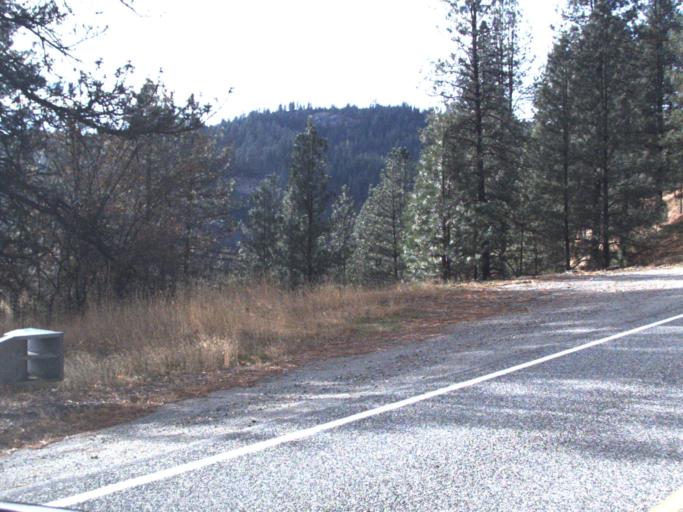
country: US
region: Washington
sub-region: Stevens County
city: Kettle Falls
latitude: 48.8002
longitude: -118.0026
